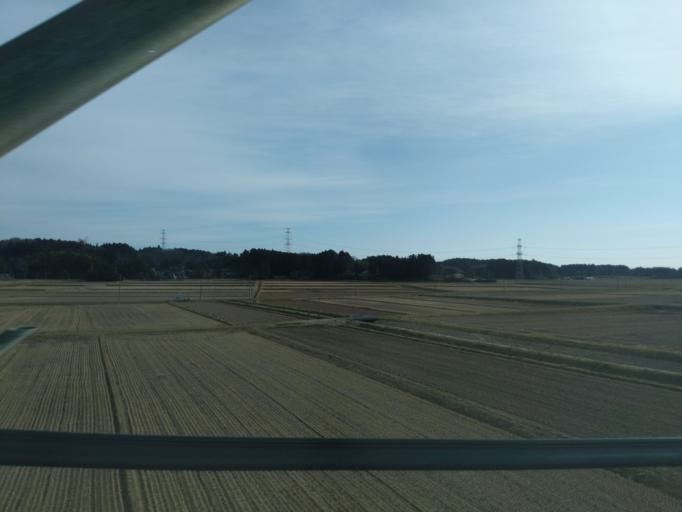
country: JP
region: Miyagi
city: Furukawa
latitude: 38.6246
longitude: 140.9999
